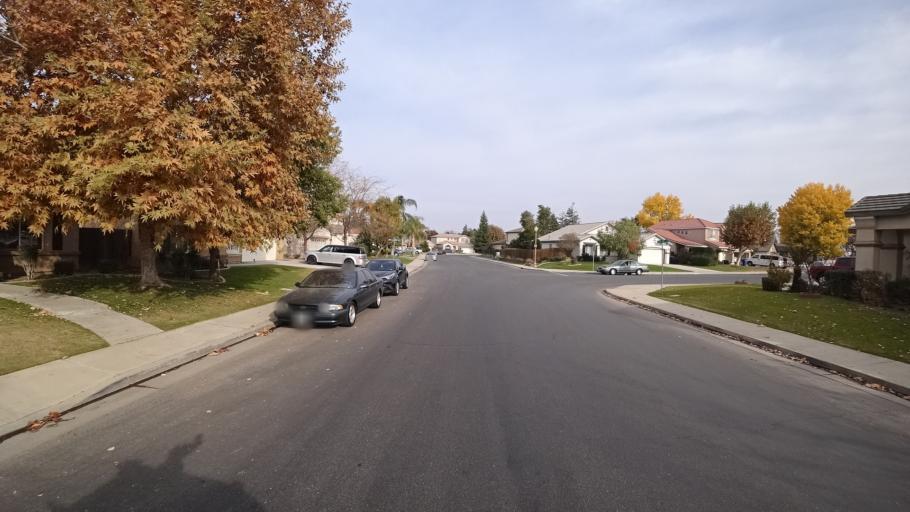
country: US
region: California
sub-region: Kern County
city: Rosedale
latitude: 35.3422
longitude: -119.1415
